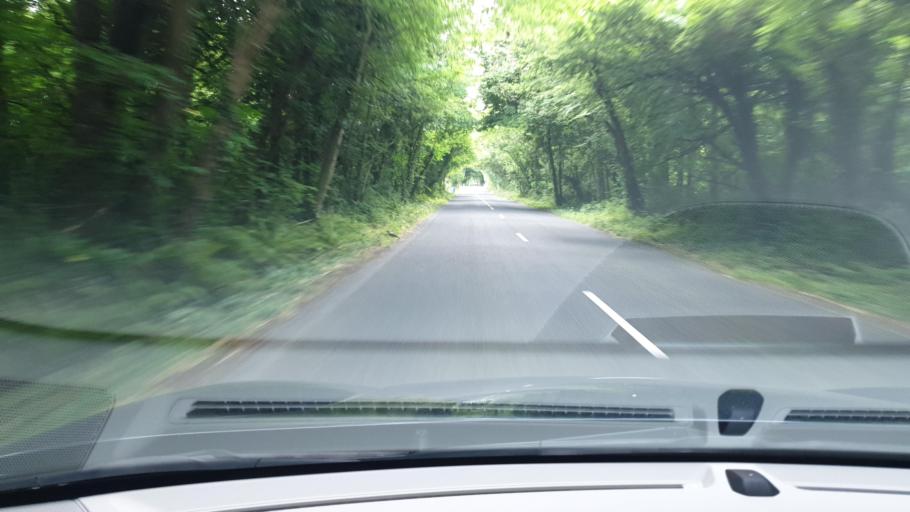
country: IE
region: Leinster
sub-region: An Mhi
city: Dunshaughlin
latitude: 53.5631
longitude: -6.5893
